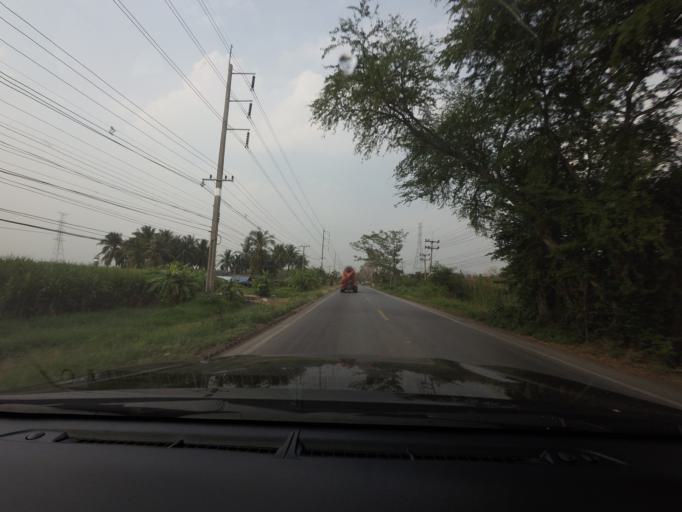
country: TH
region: Sara Buri
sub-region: Amphoe Wang Muang
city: Wang Muang
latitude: 14.8287
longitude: 101.1221
